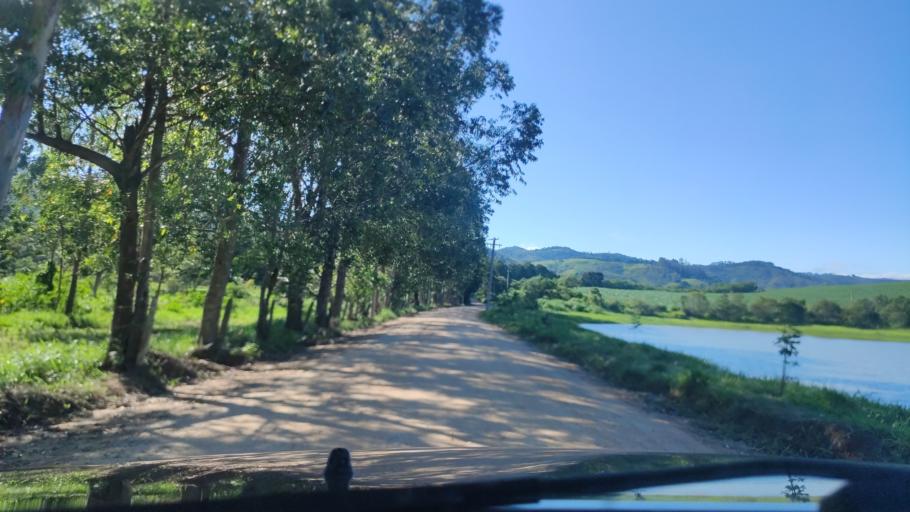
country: BR
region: Sao Paulo
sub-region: Serra Negra
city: Serra Negra
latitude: -22.5968
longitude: -46.6284
